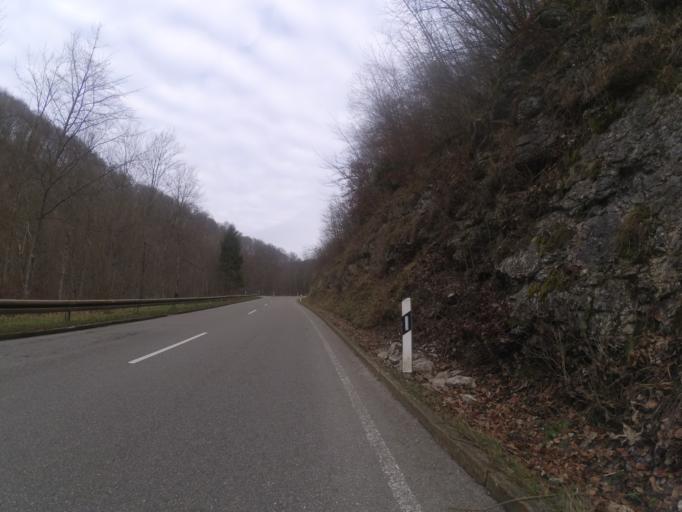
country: DE
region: Baden-Wuerttemberg
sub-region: Tuebingen Region
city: Munsingen
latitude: 48.3441
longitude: 9.4994
